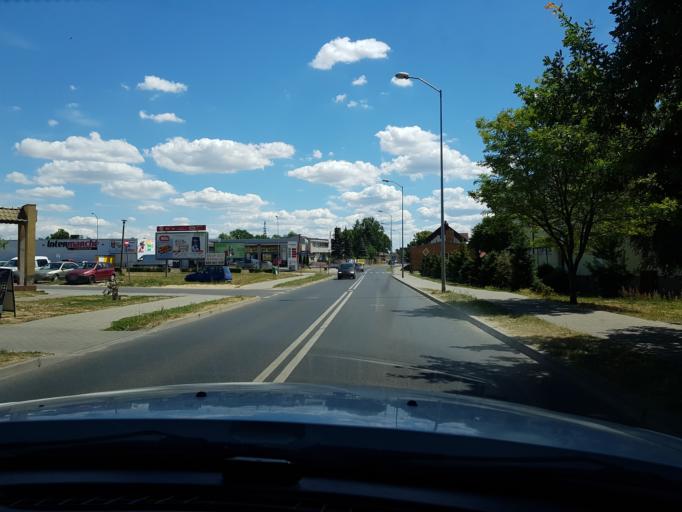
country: PL
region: West Pomeranian Voivodeship
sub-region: Powiat mysliborski
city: Mysliborz
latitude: 52.9241
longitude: 14.8762
